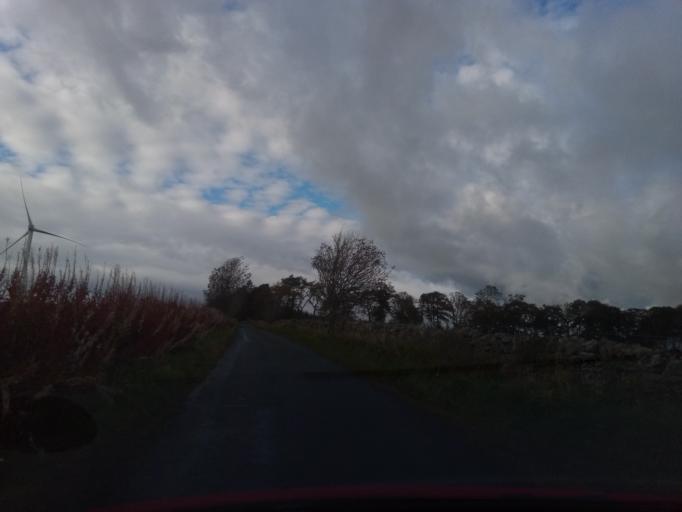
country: GB
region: Scotland
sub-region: The Scottish Borders
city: Galashiels
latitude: 55.6847
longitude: -2.8459
